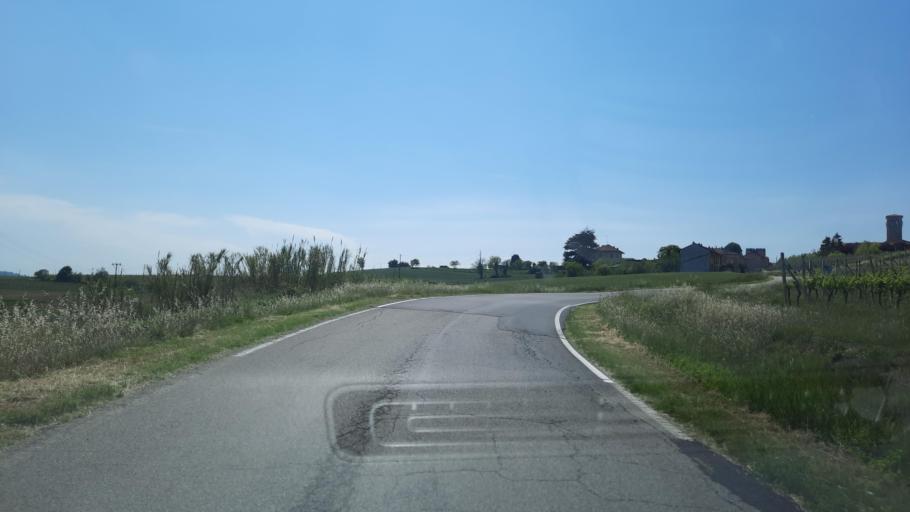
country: IT
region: Piedmont
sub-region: Provincia di Alessandria
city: Alfiano Natta
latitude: 45.0522
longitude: 8.1957
